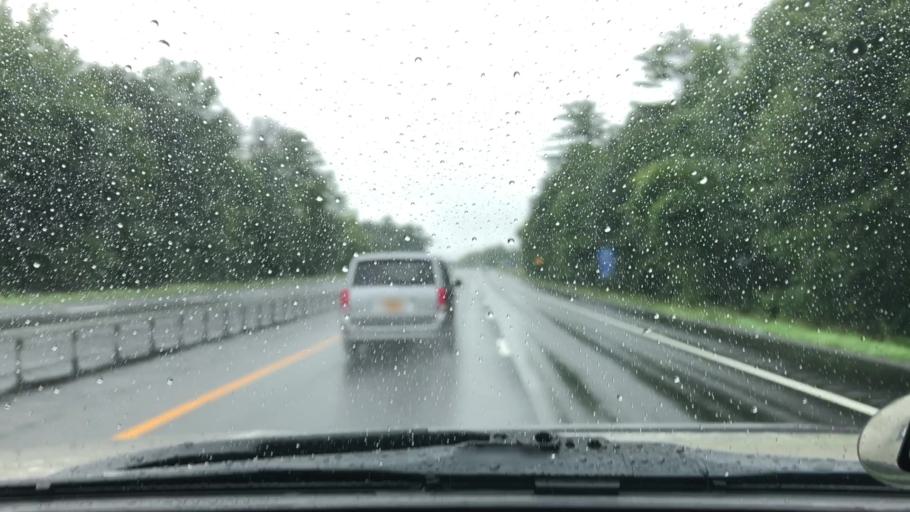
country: US
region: New York
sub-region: Greene County
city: Cairo
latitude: 42.2985
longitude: -73.9908
